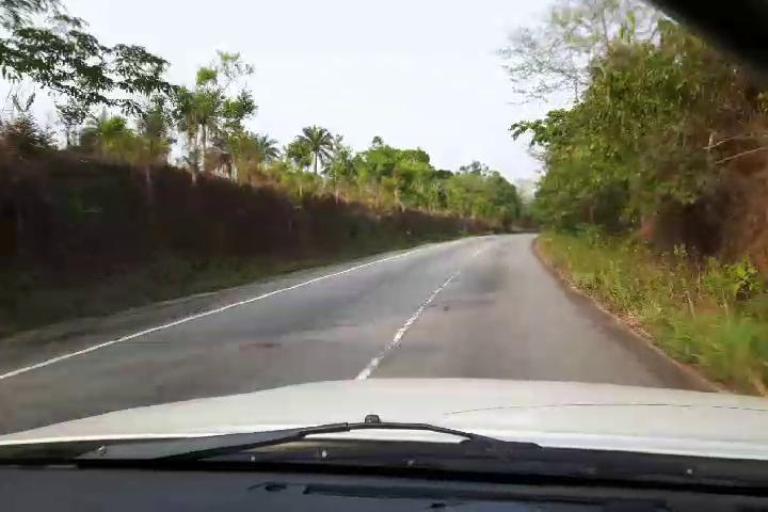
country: SL
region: Southern Province
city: Palima
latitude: 7.9321
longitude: -11.5256
